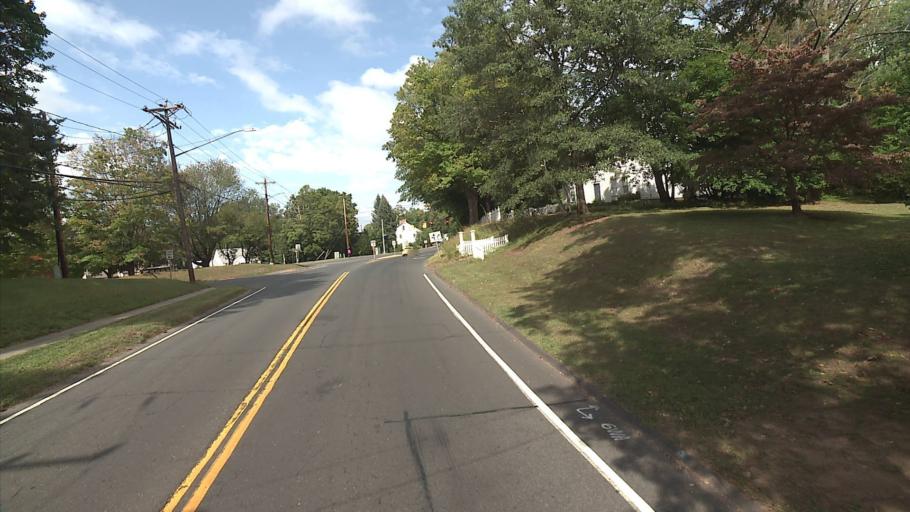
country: US
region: Connecticut
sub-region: Hartford County
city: Newington
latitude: 41.6853
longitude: -72.7219
